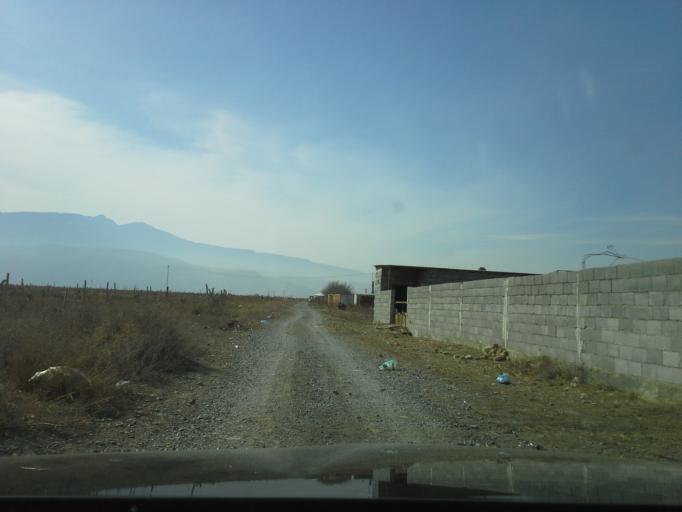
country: TM
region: Ahal
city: Abadan
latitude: 38.1218
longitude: 58.0031
